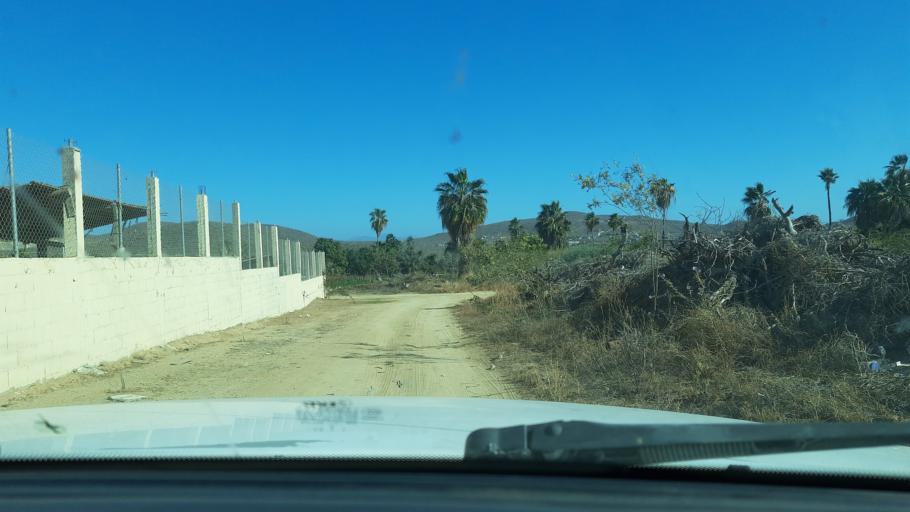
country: MX
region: Baja California Sur
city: Todos Santos
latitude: 23.4722
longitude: -110.2197
